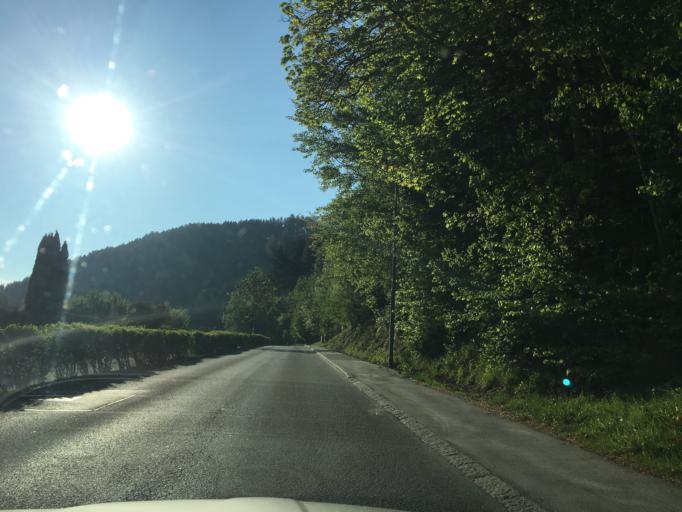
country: AT
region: Tyrol
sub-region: Politischer Bezirk Innsbruck Land
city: Ampass
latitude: 47.2602
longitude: 11.4430
